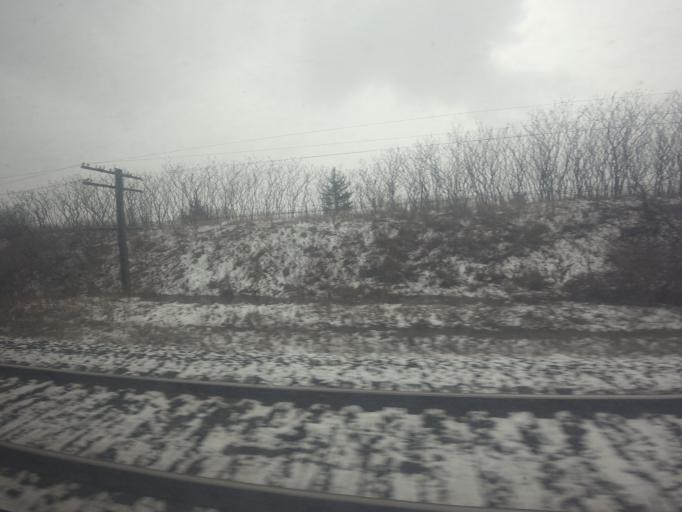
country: CA
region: Ontario
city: Quinte West
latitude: 44.0954
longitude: -77.6226
